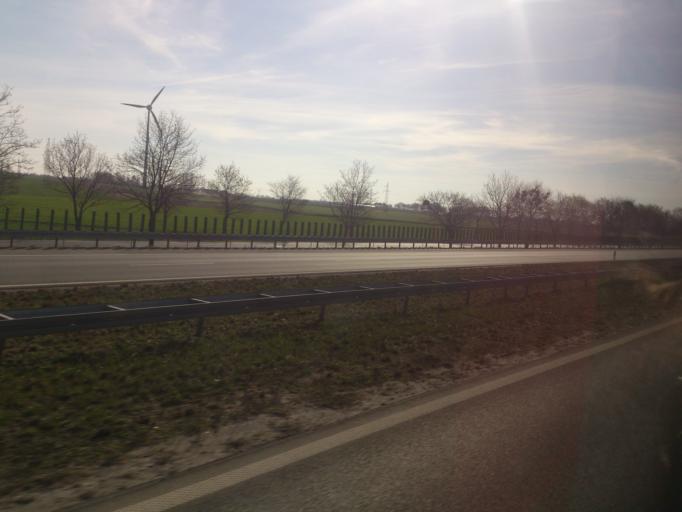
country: PL
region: Kujawsko-Pomorskie
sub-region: Powiat aleksandrowski
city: Raciazek
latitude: 52.8487
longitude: 18.7832
